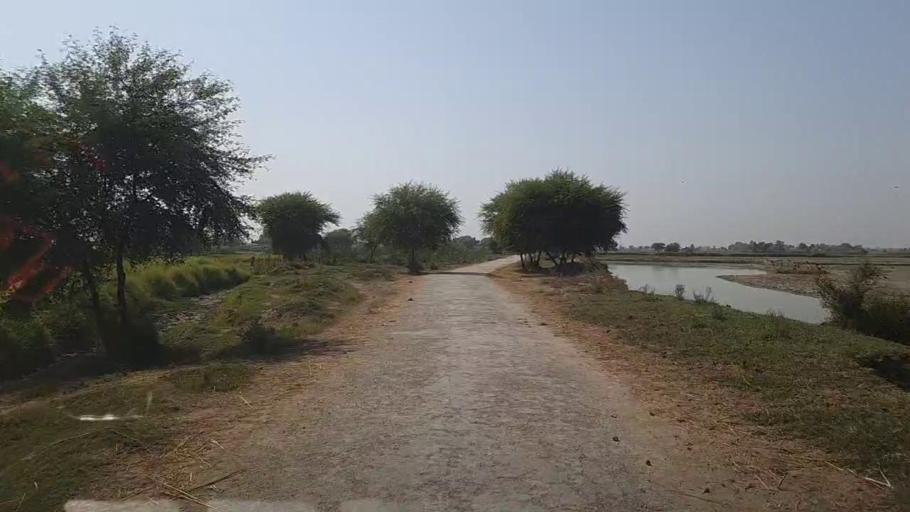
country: PK
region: Sindh
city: Kandhkot
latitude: 28.3844
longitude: 69.3162
